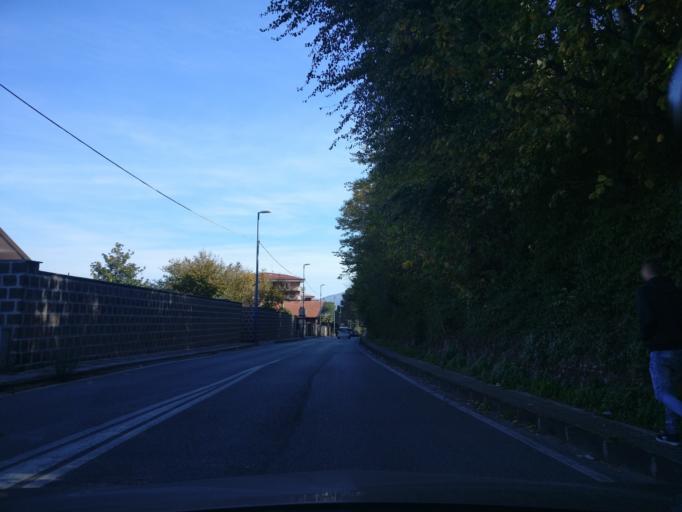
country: IT
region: Campania
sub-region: Provincia di Avellino
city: Torelli-Torrette
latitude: 40.9132
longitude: 14.7654
